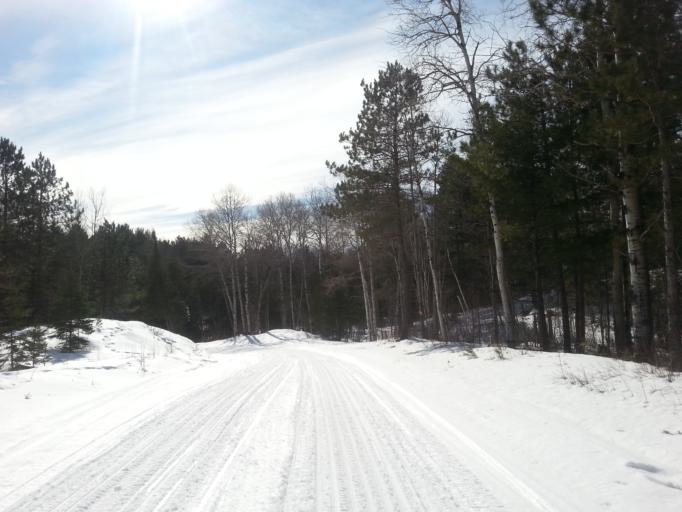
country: CA
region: Ontario
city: Greater Sudbury
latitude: 46.3368
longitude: -80.9047
